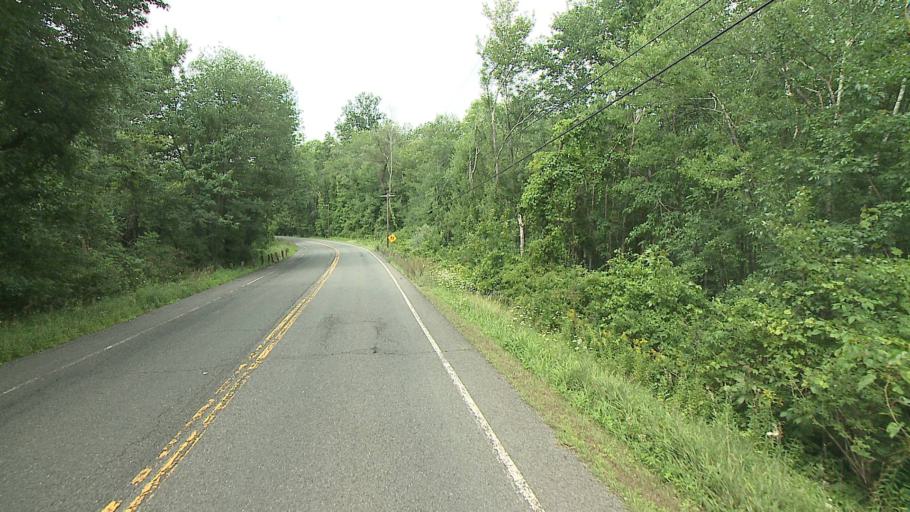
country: US
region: Connecticut
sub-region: Fairfield County
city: Sherman
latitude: 41.6475
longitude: -73.5148
